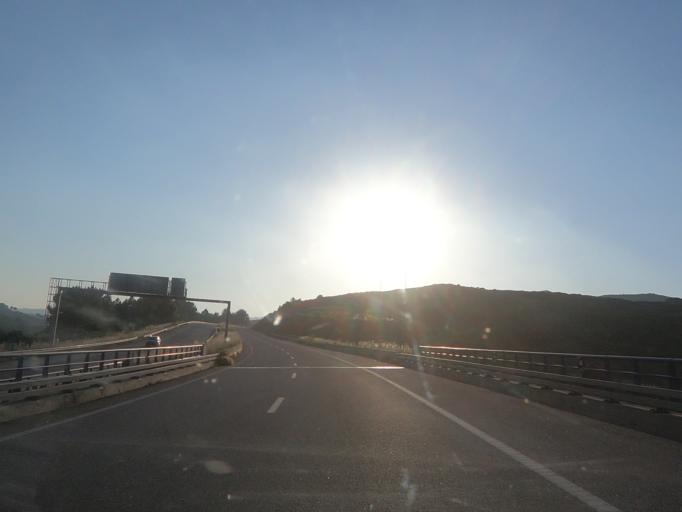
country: PT
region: Guarda
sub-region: Celorico da Beira
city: Celorico da Beira
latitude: 40.6323
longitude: -7.4337
